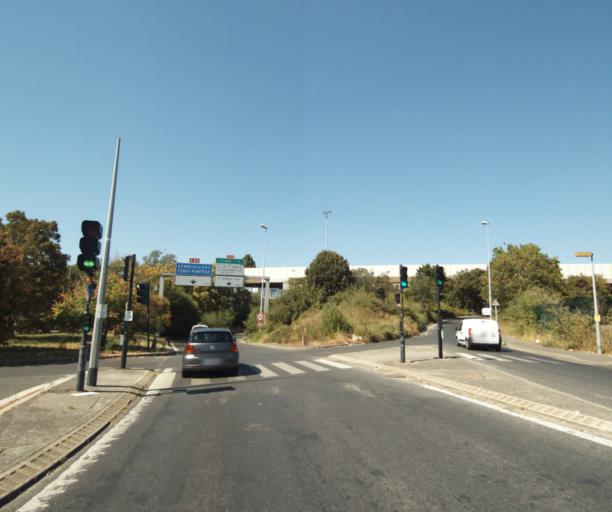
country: FR
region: Ile-de-France
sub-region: Departement de Seine-Saint-Denis
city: Saint-Denis
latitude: 48.9215
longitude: 2.3467
